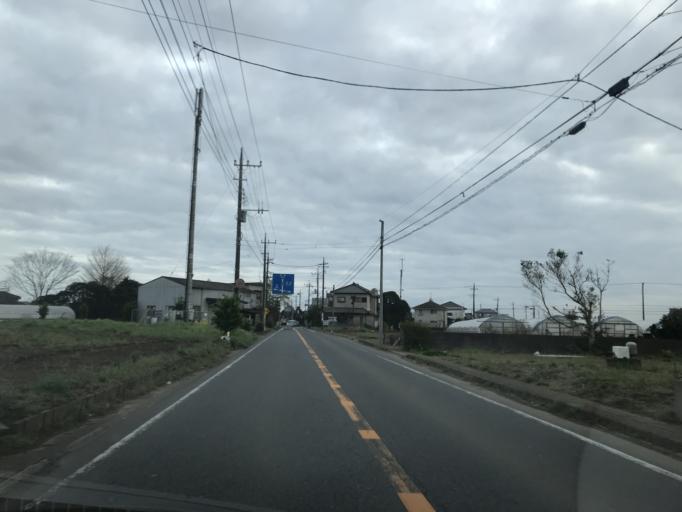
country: JP
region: Chiba
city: Omigawa
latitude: 35.7888
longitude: 140.6069
